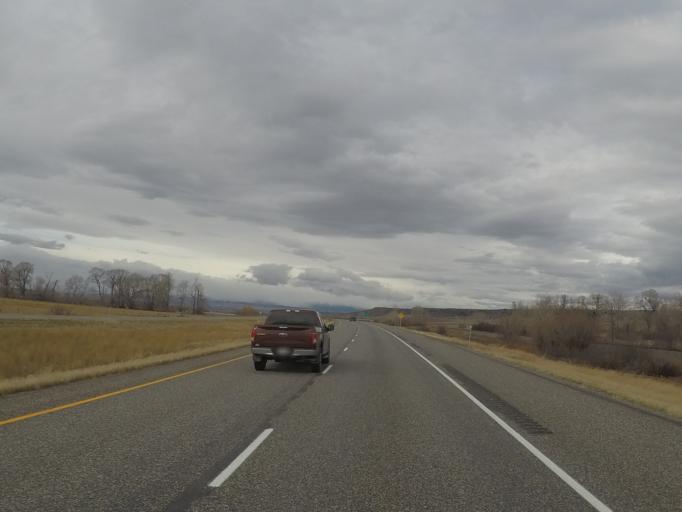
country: US
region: Montana
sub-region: Sweet Grass County
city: Big Timber
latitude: 45.7768
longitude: -109.8005
